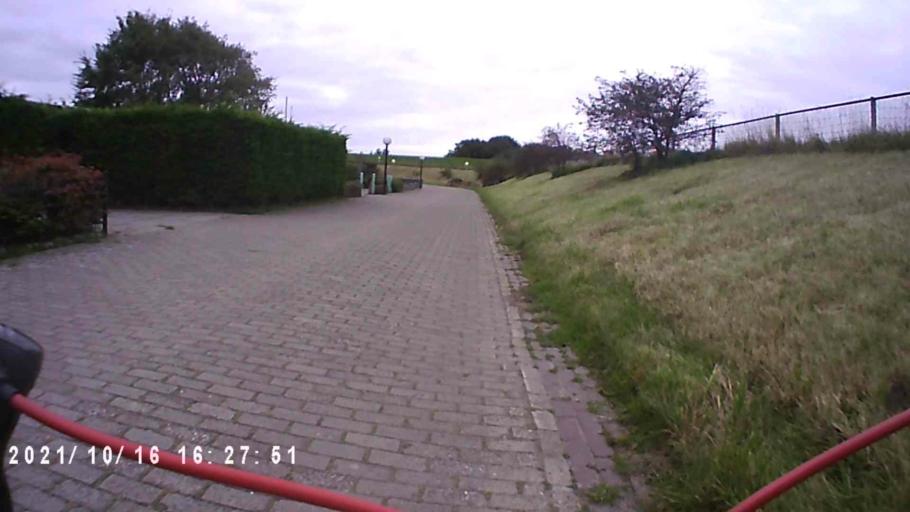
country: NL
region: Friesland
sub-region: Gemeente Dongeradeel
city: Anjum
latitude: 53.3831
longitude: 6.1555
